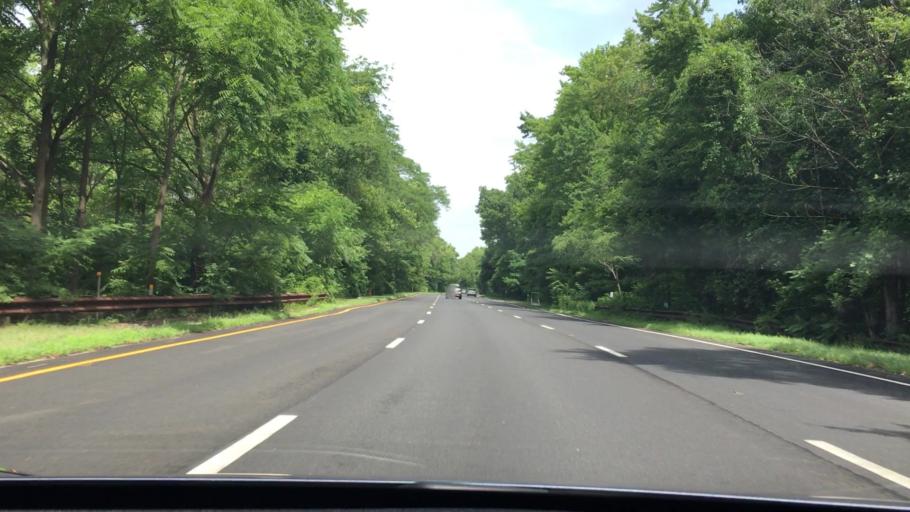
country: US
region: New York
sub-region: Nassau County
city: Wantagh
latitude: 40.6789
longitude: -73.5128
